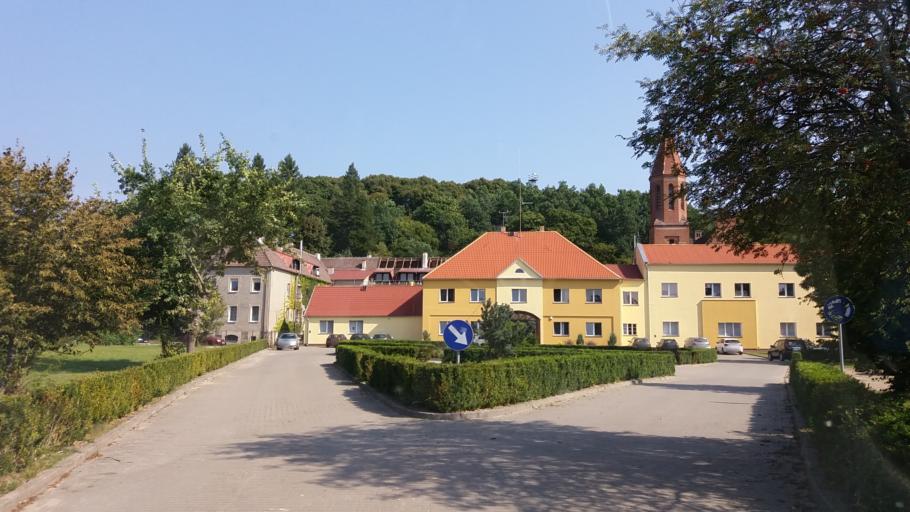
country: PL
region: Greater Poland Voivodeship
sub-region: Powiat czarnkowsko-trzcianecki
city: Krzyz Wielkopolski
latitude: 53.0470
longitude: 15.9444
